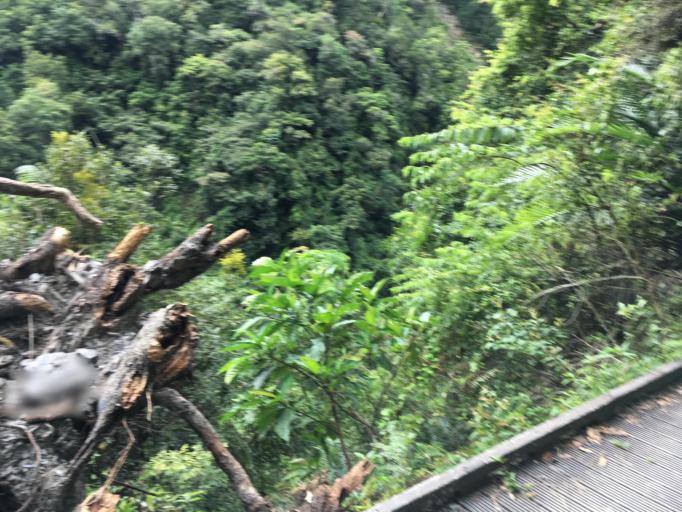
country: TW
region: Taiwan
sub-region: Yilan
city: Yilan
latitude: 24.4246
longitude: 121.7004
